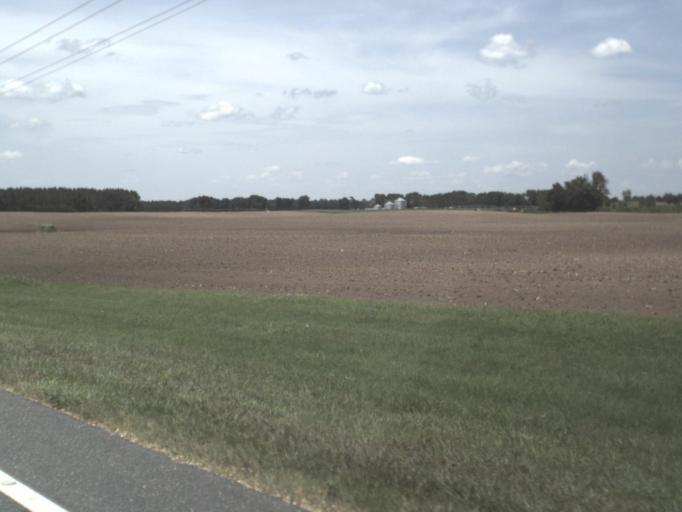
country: US
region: Florida
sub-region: Gilchrist County
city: Trenton
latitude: 29.8252
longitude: -82.8672
